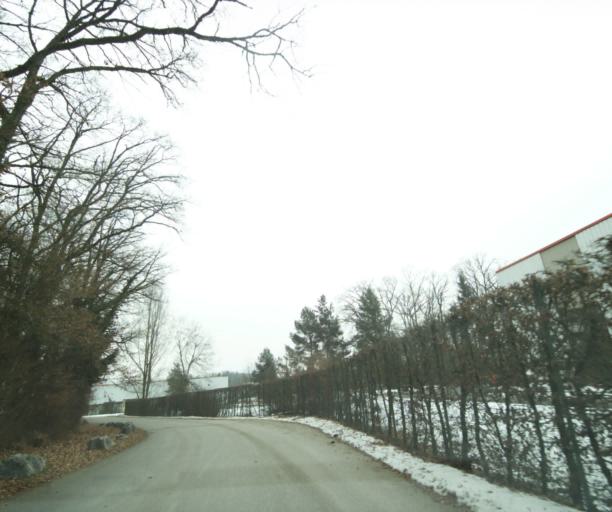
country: FR
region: Rhone-Alpes
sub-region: Departement de la Haute-Savoie
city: Reignier-Esery
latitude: 46.1359
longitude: 6.2974
